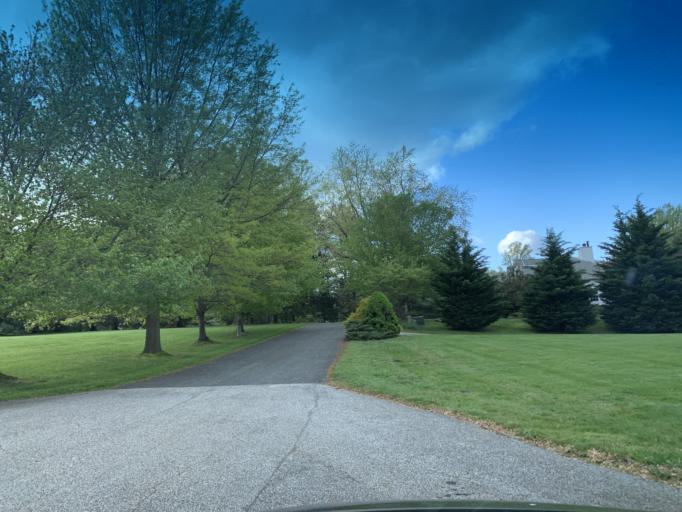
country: US
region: Maryland
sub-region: Baltimore County
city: Hunt Valley
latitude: 39.5243
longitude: -76.5517
